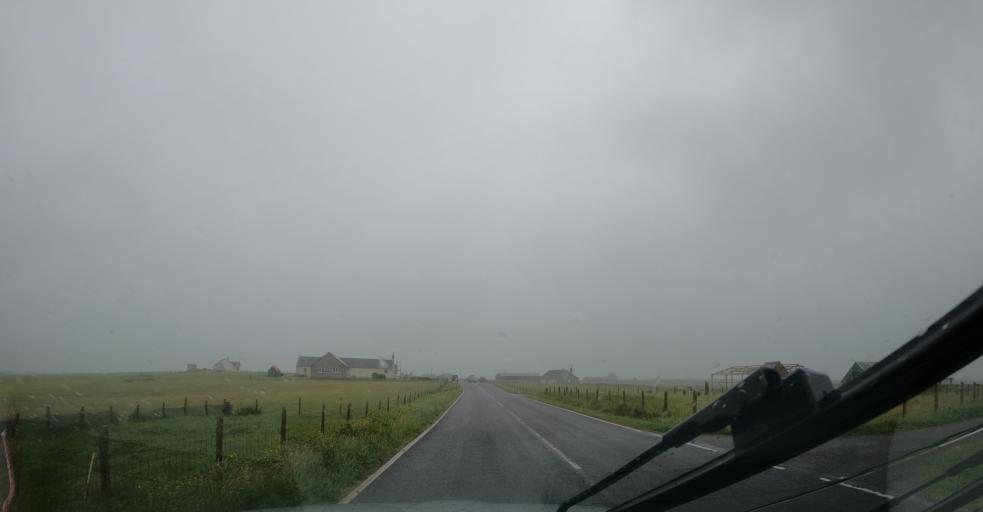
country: GB
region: Scotland
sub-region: Eilean Siar
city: Benbecula
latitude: 57.4565
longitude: -7.3973
